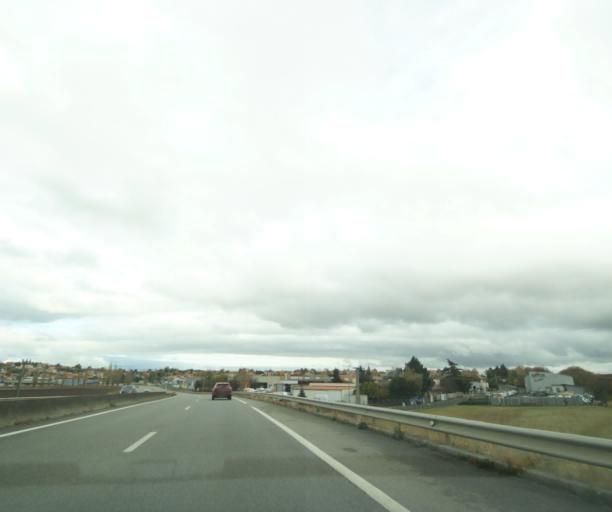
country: FR
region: Auvergne
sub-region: Departement du Puy-de-Dome
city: Dallet
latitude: 45.7894
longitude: 3.2236
